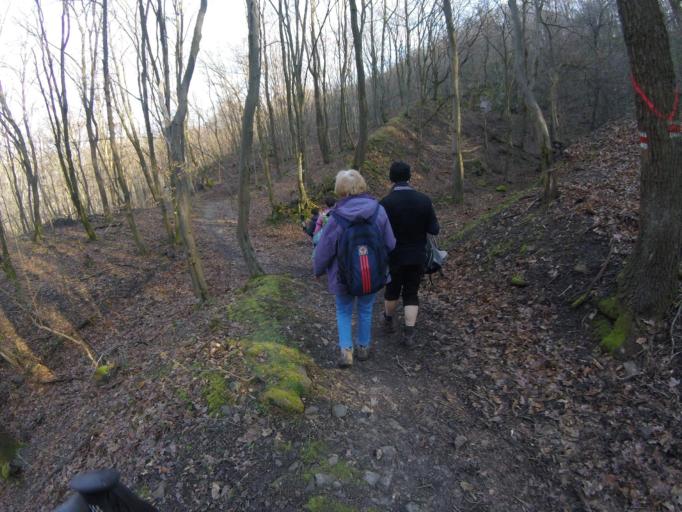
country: HU
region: Komarom-Esztergom
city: Pilismarot
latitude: 47.7554
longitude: 18.8927
